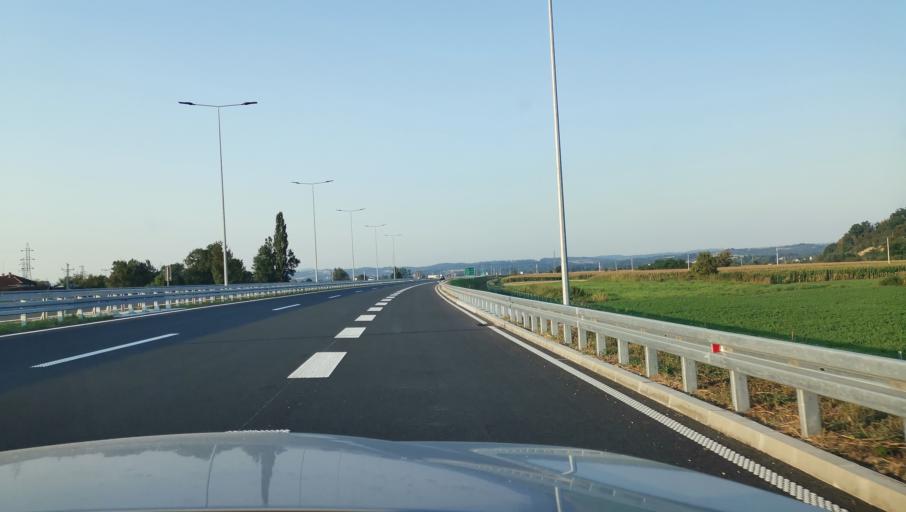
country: RS
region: Central Serbia
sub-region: Kolubarski Okrug
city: Ljig
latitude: 44.2361
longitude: 20.2564
